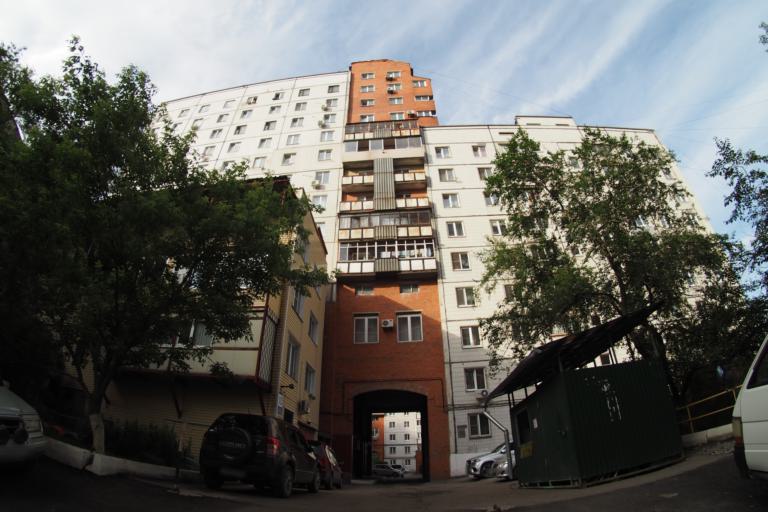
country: RU
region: Primorskiy
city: Vladivostok
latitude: 43.1160
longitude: 131.9339
